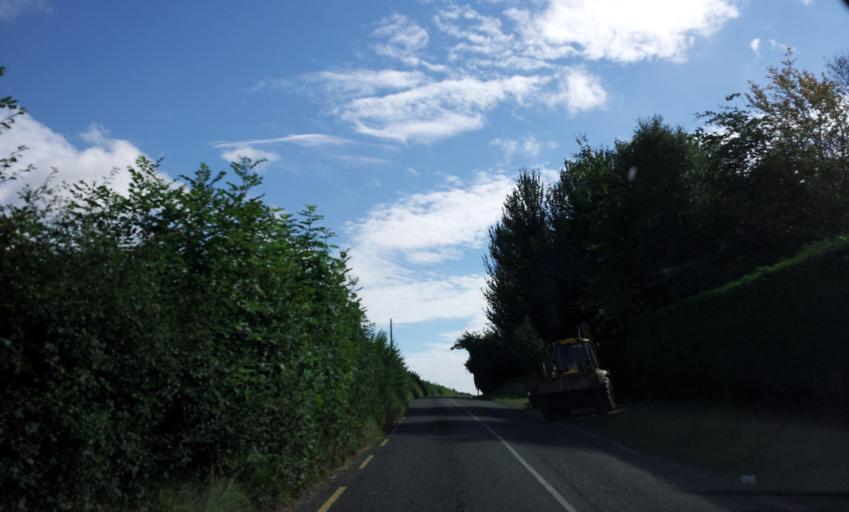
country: IE
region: Leinster
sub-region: Laois
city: Portlaoise
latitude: 53.0133
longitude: -7.2514
